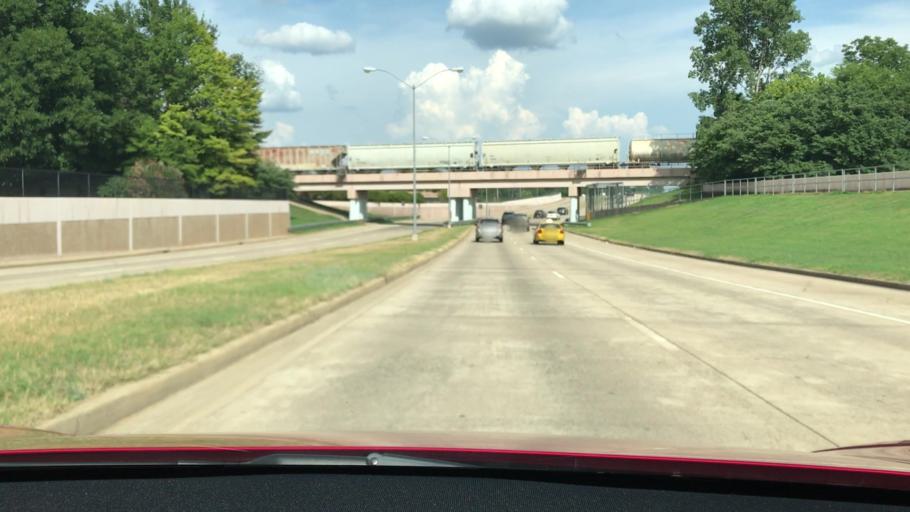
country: US
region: Louisiana
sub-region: Bossier Parish
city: Bossier City
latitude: 32.5115
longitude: -93.7245
